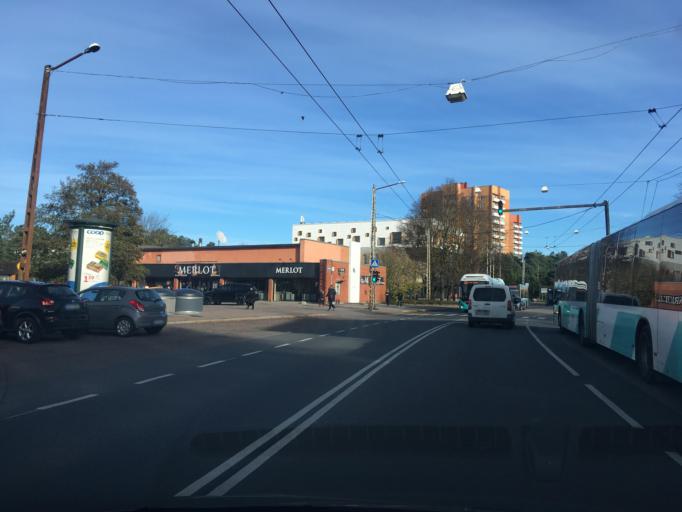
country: EE
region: Harju
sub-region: Saue vald
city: Laagri
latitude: 59.4033
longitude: 24.6643
